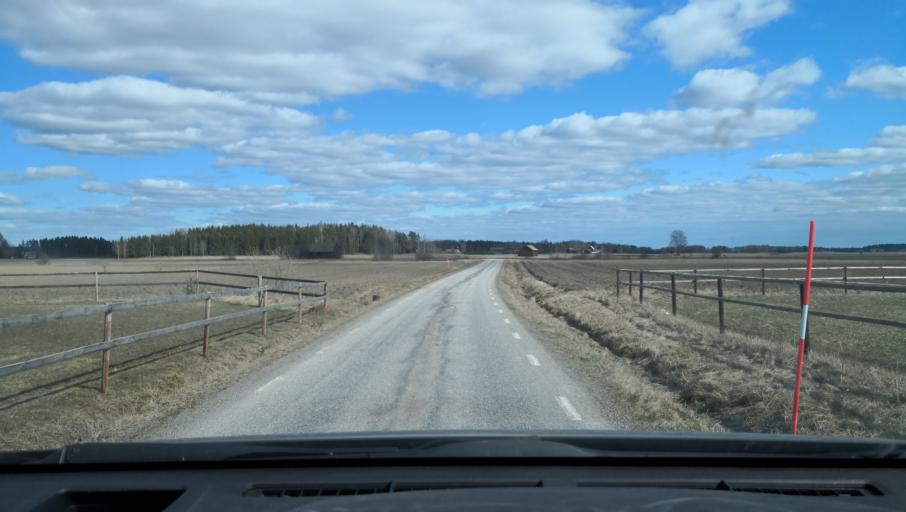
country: SE
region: Vaestmanland
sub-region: Sala Kommun
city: Sala
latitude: 59.8617
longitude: 16.5776
